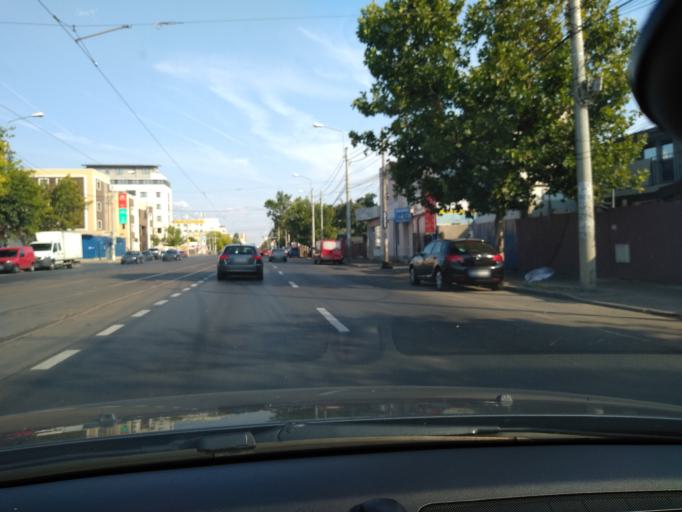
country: RO
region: Ilfov
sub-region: Comuna Chiajna
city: Rosu
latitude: 44.4816
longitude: 26.0317
